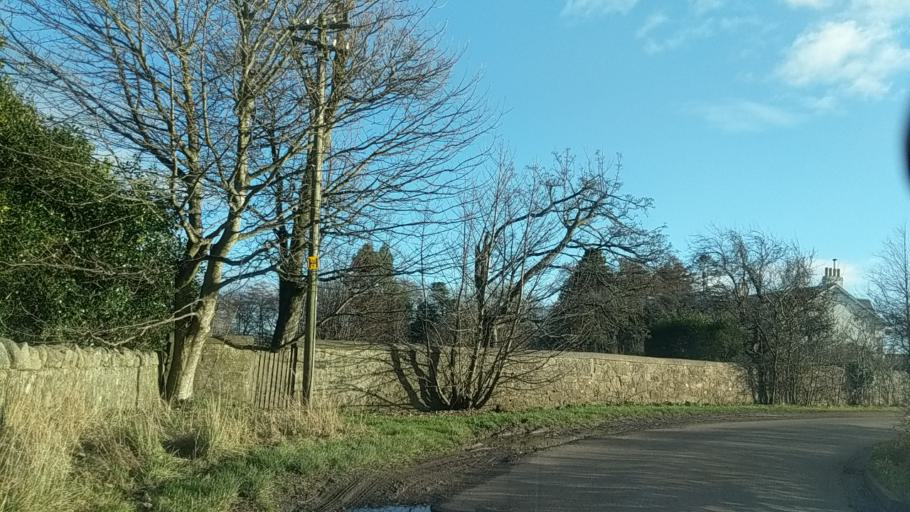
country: GB
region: Scotland
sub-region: West Lothian
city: Broxburn
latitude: 55.9736
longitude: -3.4462
